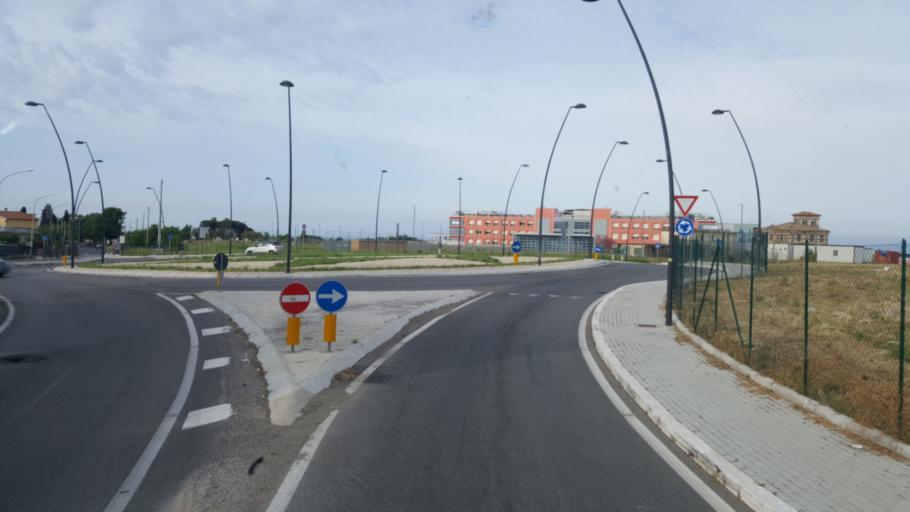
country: IT
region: Latium
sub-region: Citta metropolitana di Roma Capitale
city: Cecchina
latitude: 41.6792
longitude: 12.6513
